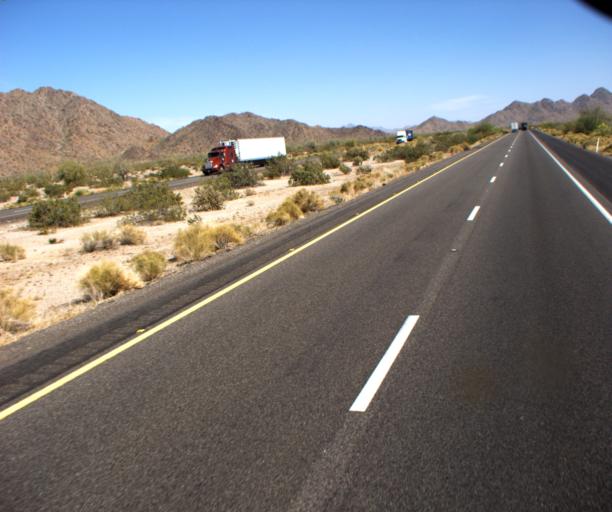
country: US
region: Arizona
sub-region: Maricopa County
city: Gila Bend
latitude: 32.9072
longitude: -112.5895
